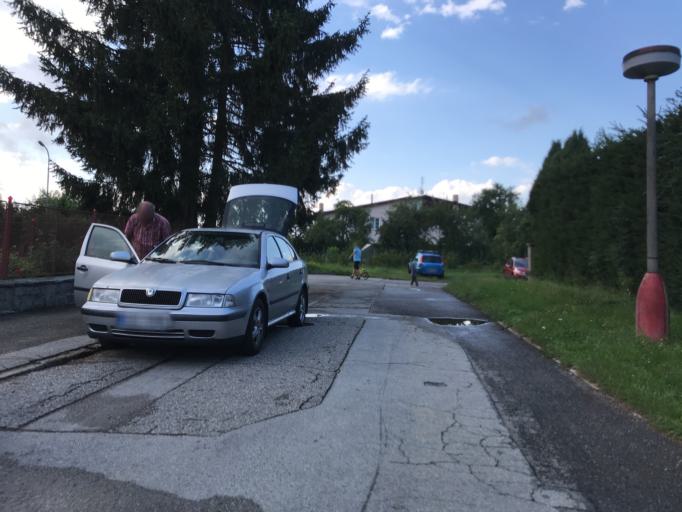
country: CZ
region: Jihocesky
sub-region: Okres Jindrichuv Hradec
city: Trebon
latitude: 49.0085
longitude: 14.7528
